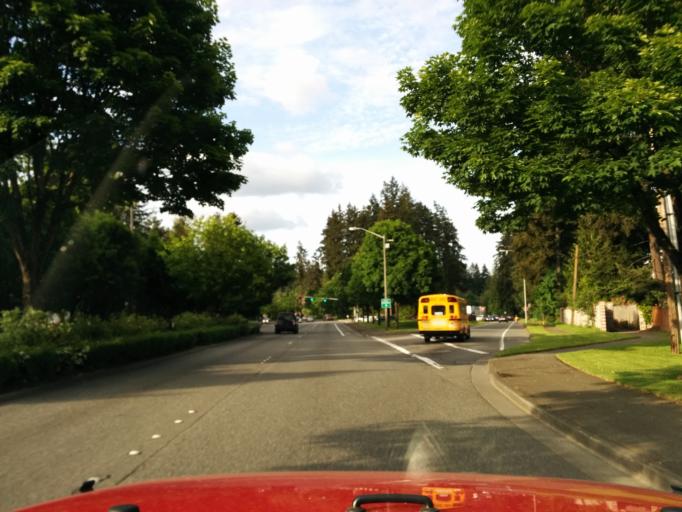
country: US
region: Washington
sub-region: King County
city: Redmond
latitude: 47.6865
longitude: -122.0944
